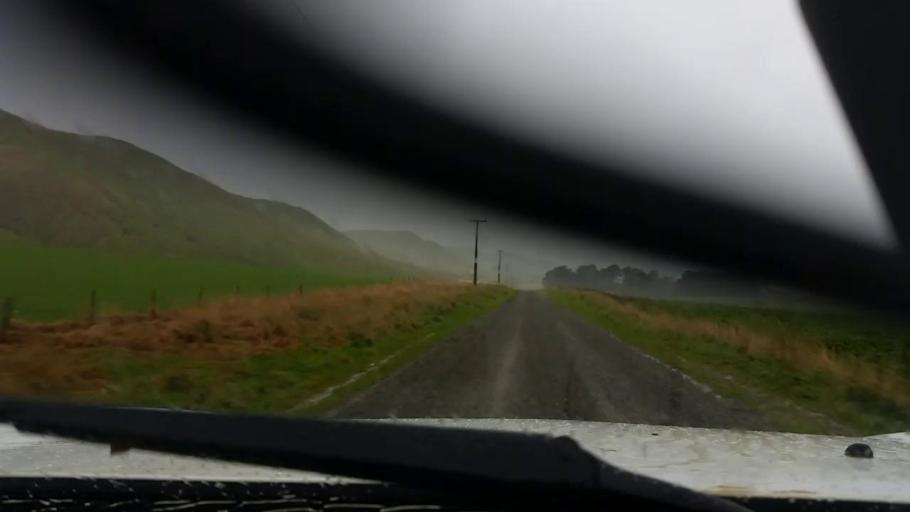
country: NZ
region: Wellington
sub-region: Masterton District
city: Masterton
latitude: -41.2561
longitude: 175.9063
